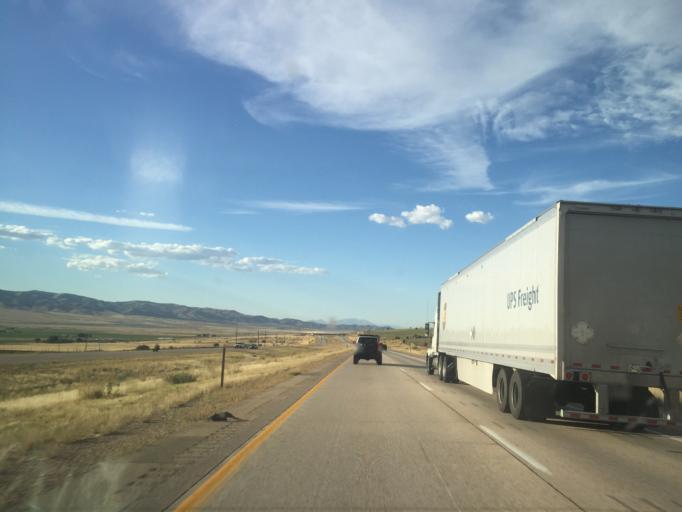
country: US
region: Utah
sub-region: Juab County
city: Nephi
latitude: 39.7326
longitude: -111.8248
